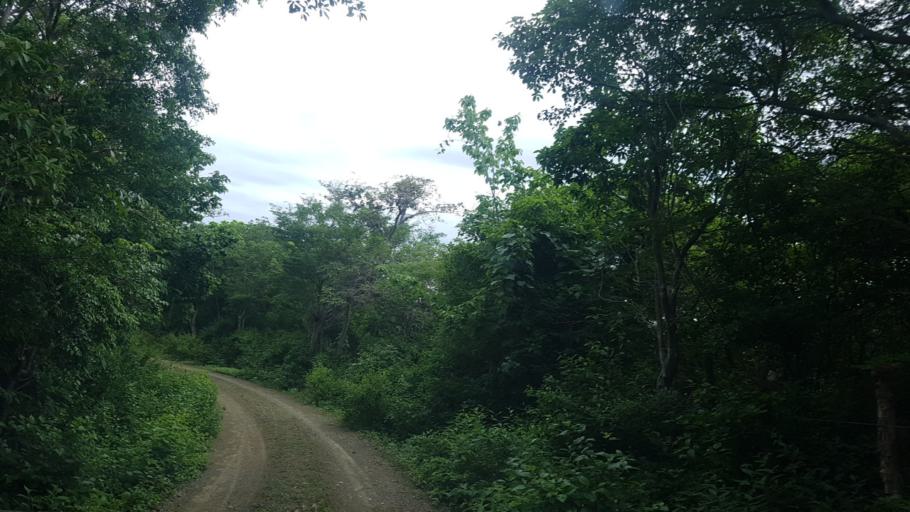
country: NI
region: Nueva Segovia
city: Ciudad Antigua
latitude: 13.5949
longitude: -86.3693
